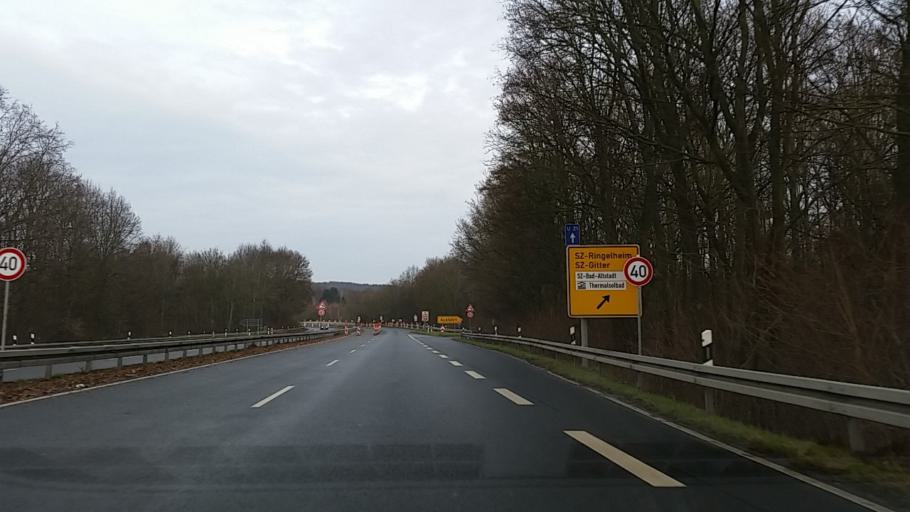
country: DE
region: Lower Saxony
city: Alt Wallmoden
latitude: 52.0408
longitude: 10.3568
